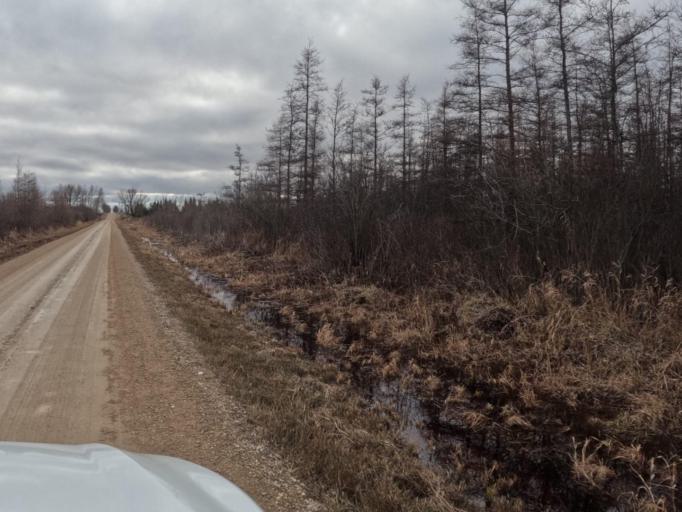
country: CA
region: Ontario
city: Shelburne
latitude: 43.8985
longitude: -80.4083
